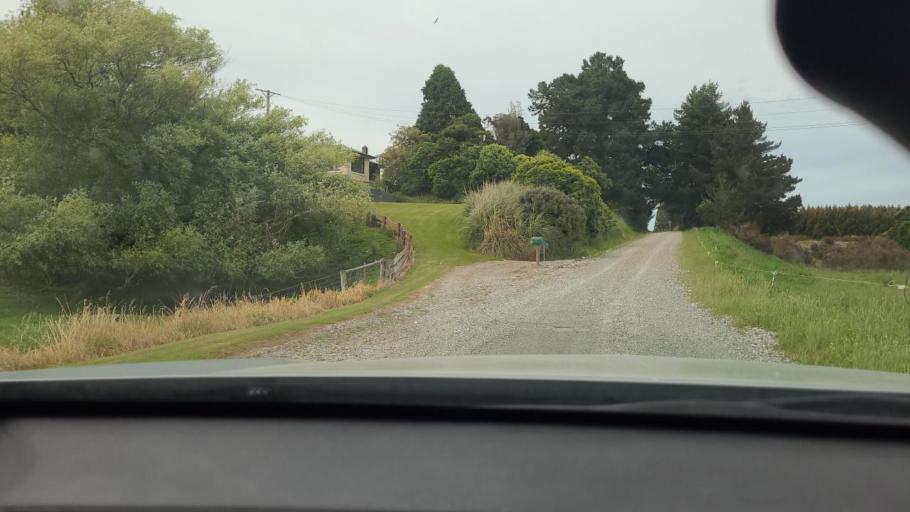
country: NZ
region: Southland
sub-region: Southland District
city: Riverton
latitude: -46.1665
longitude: 167.6823
